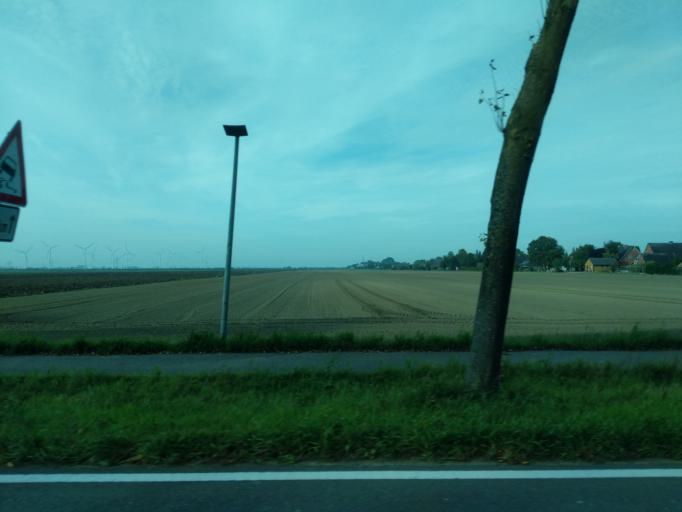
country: DE
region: Schleswig-Holstein
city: Rethwisch
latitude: 53.8653
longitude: 9.5921
